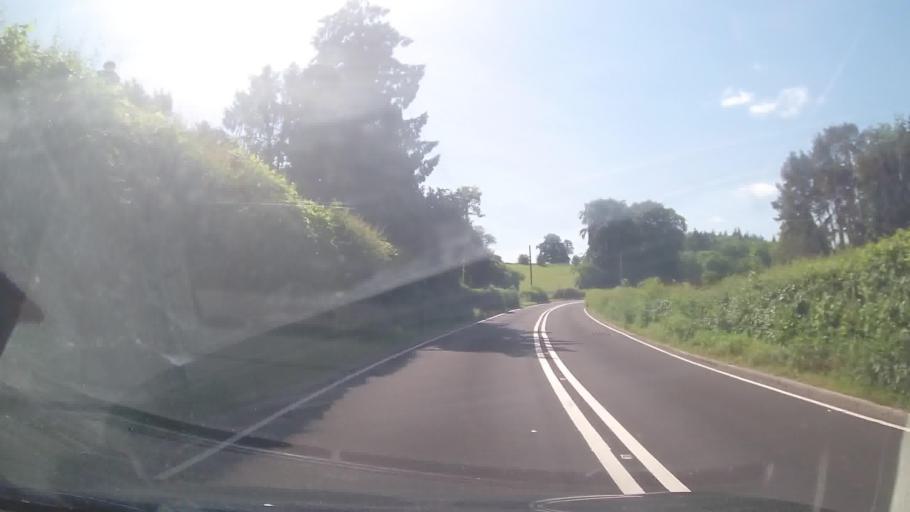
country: GB
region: England
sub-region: Herefordshire
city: Kimbolton
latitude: 52.2733
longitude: -2.7104
